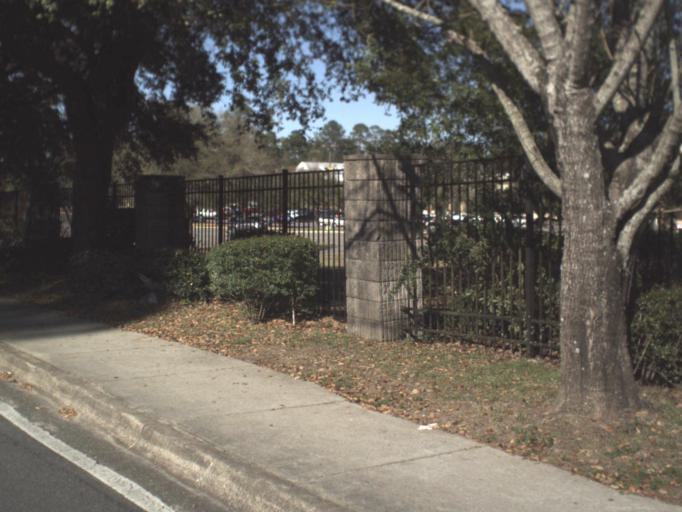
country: US
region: Florida
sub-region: Leon County
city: Tallahassee
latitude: 30.4399
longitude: -84.2617
